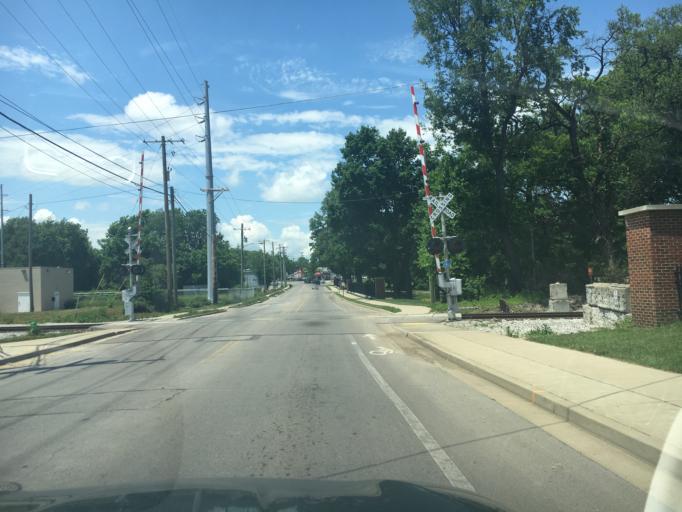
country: US
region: Kentucky
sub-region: Fayette County
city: Mount Vernon
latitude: 38.0584
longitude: -84.4987
